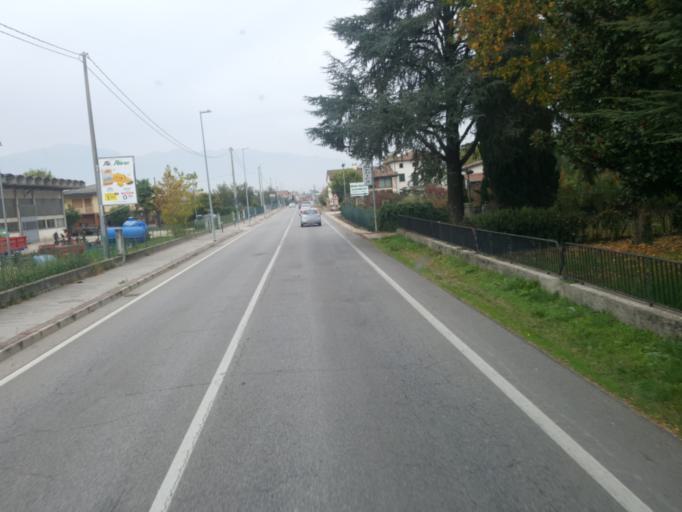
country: IT
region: Veneto
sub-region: Provincia di Treviso
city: Loria Bessica
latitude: 45.7353
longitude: 11.8664
